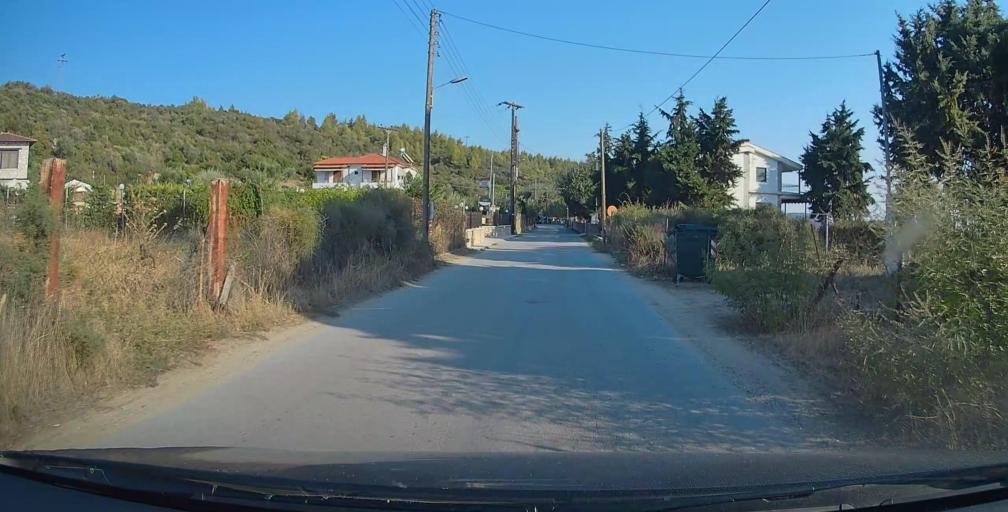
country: GR
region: Central Macedonia
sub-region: Nomos Chalkidikis
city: Sykia
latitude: 39.9959
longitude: 23.8906
